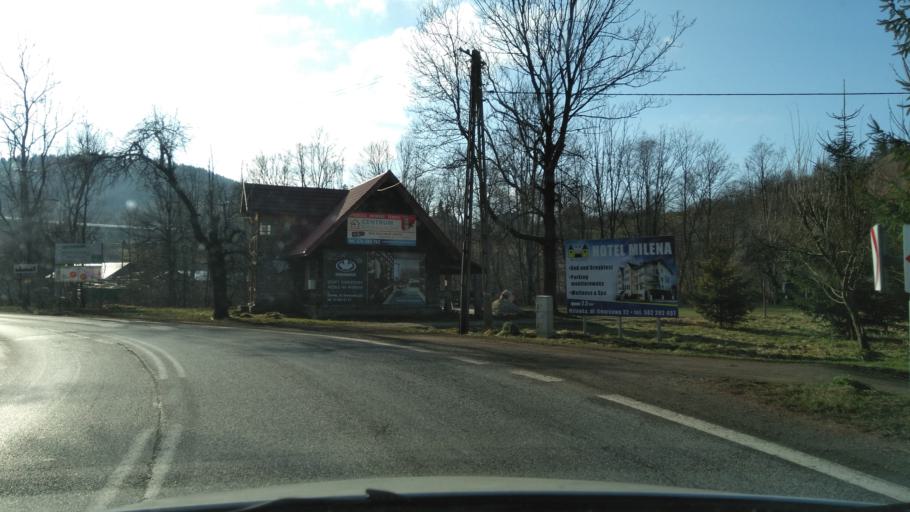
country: PL
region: Silesian Voivodeship
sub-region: Powiat zywiecki
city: Milowka
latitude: 49.5687
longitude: 19.0695
